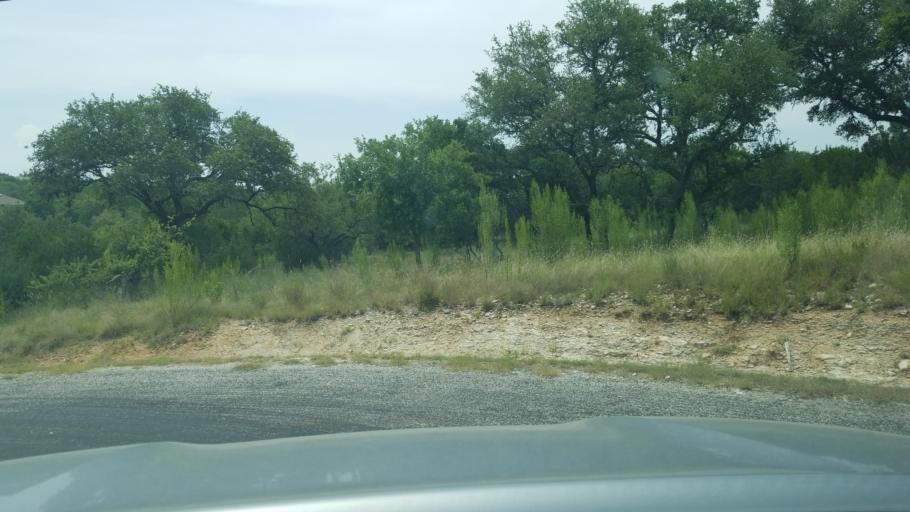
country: US
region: Texas
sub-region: Bexar County
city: Timberwood Park
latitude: 29.6866
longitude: -98.5102
